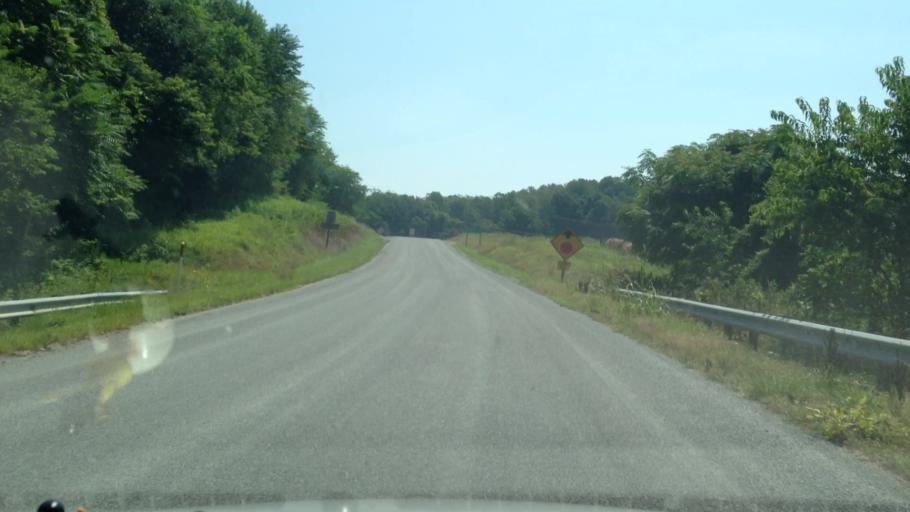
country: US
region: Virginia
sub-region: Patrick County
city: Stuart
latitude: 36.5886
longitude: -80.2830
